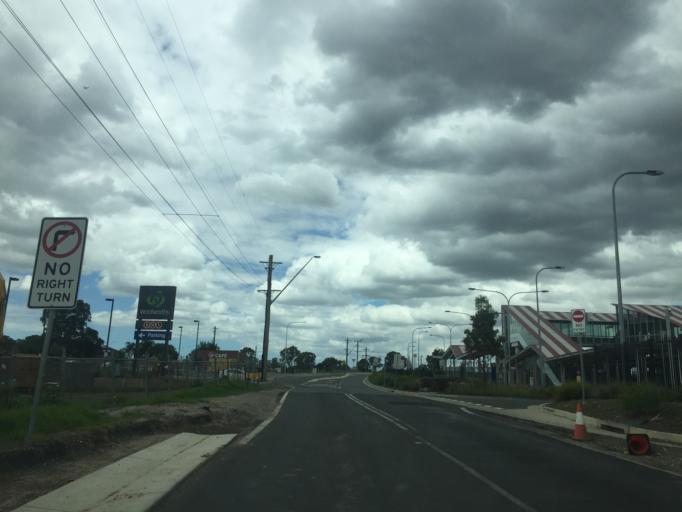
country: AU
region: New South Wales
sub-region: Blacktown
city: Riverstone
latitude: -33.7034
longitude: 150.8739
